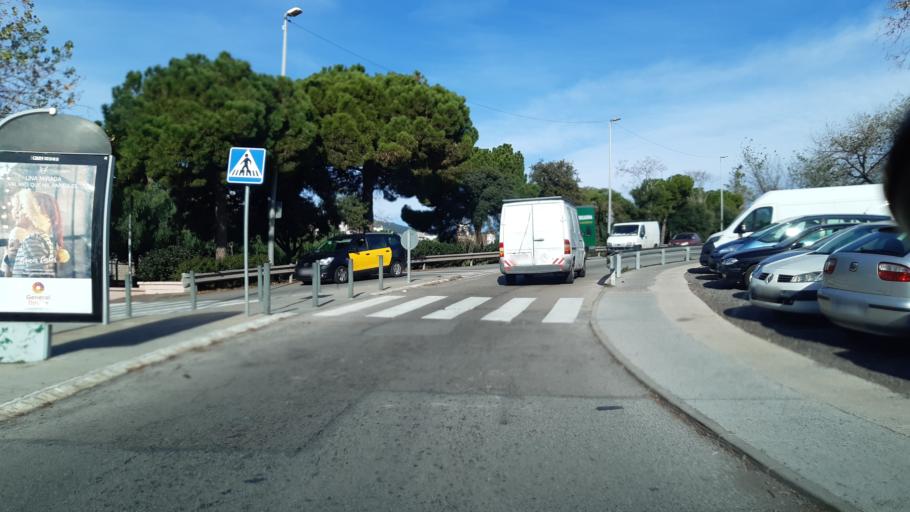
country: ES
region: Catalonia
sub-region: Provincia de Barcelona
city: L'Hospitalet de Llobregat
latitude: 41.3633
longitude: 2.1159
